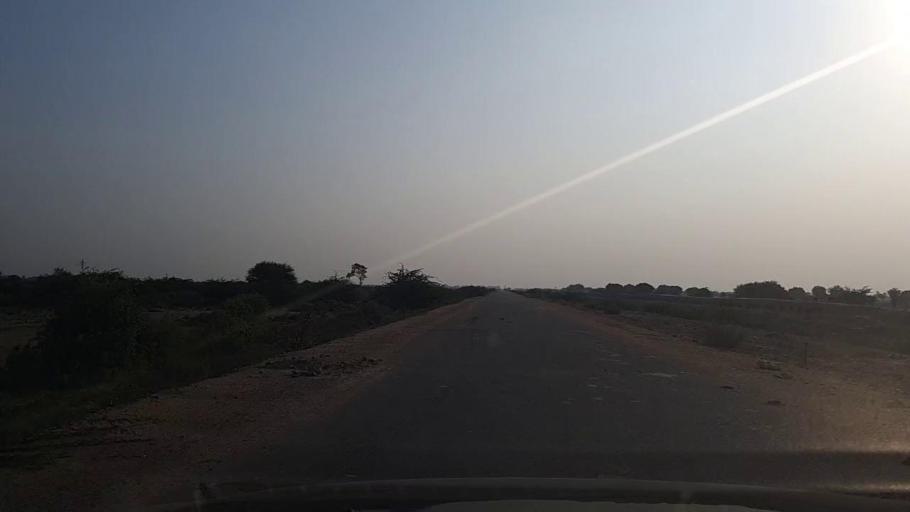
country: PK
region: Sindh
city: Mirpur Sakro
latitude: 24.4831
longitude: 67.8060
